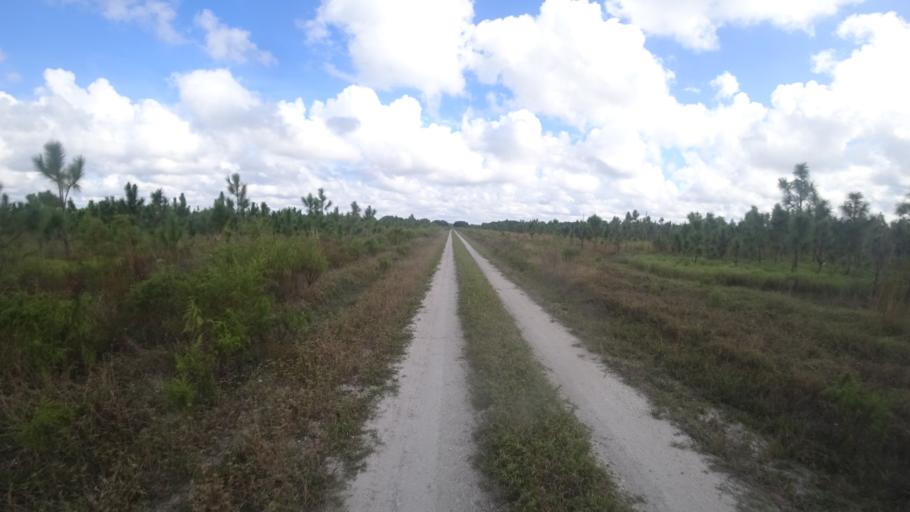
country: US
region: Florida
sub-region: Hillsborough County
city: Wimauma
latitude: 27.5054
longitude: -82.1434
